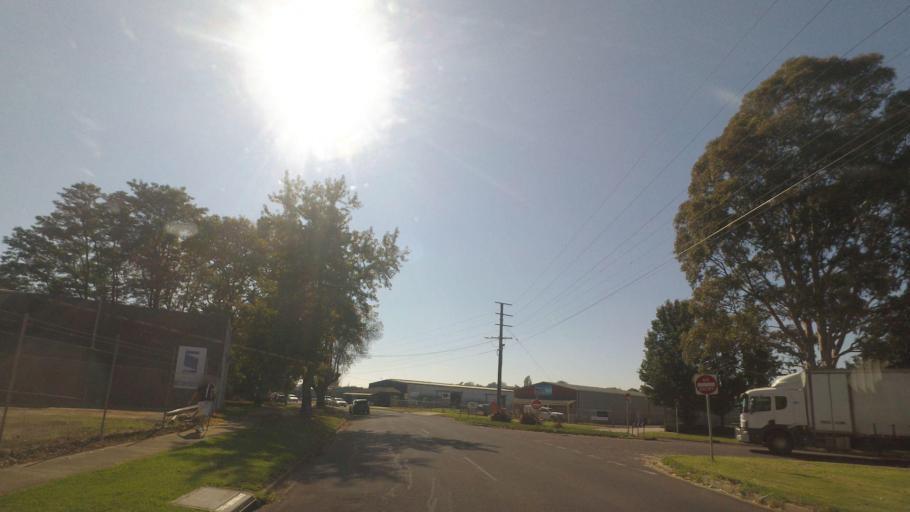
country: AU
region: Victoria
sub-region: Baw Baw
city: Warragul
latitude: -38.1650
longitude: 145.9385
